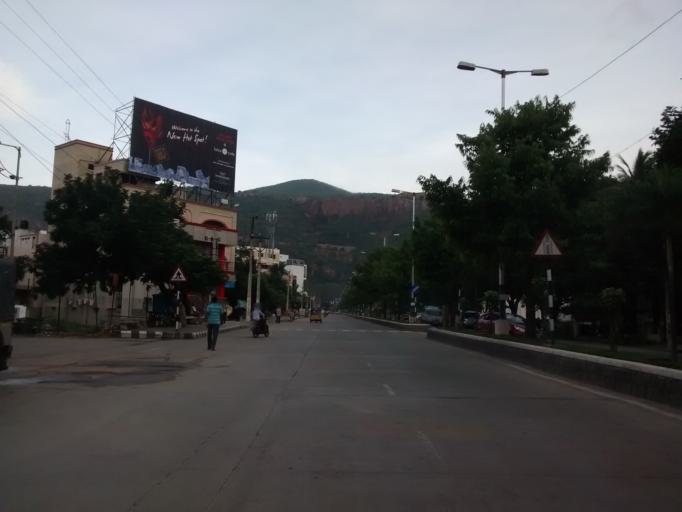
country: IN
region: Andhra Pradesh
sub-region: Chittoor
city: Akkarampalle
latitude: 13.6506
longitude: 79.4234
